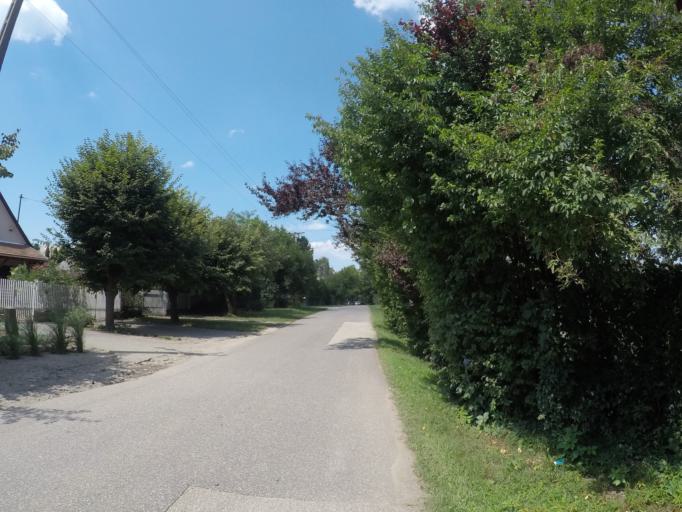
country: HU
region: Somogy
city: Balatonszabadi
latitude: 46.9296
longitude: 18.1263
